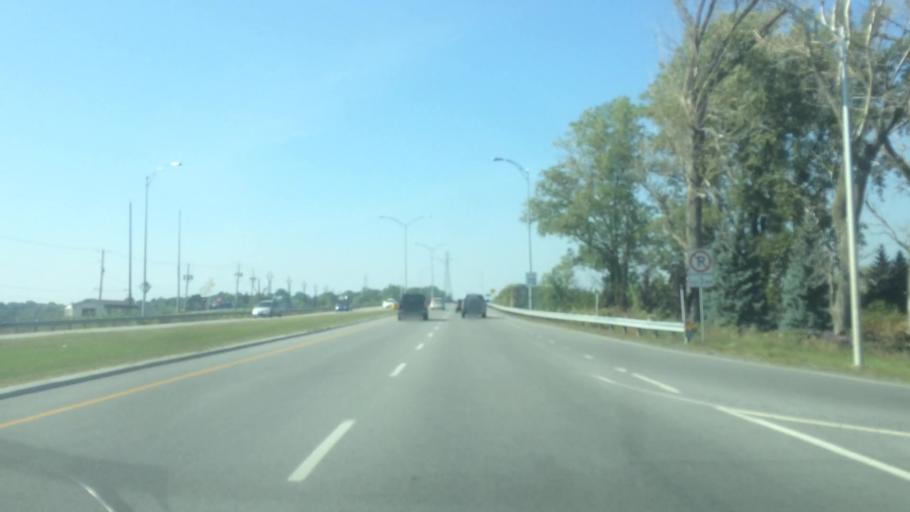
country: CA
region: Quebec
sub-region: Monteregie
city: Salaberry-de-Valleyfield
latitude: 45.2691
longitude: -74.1625
